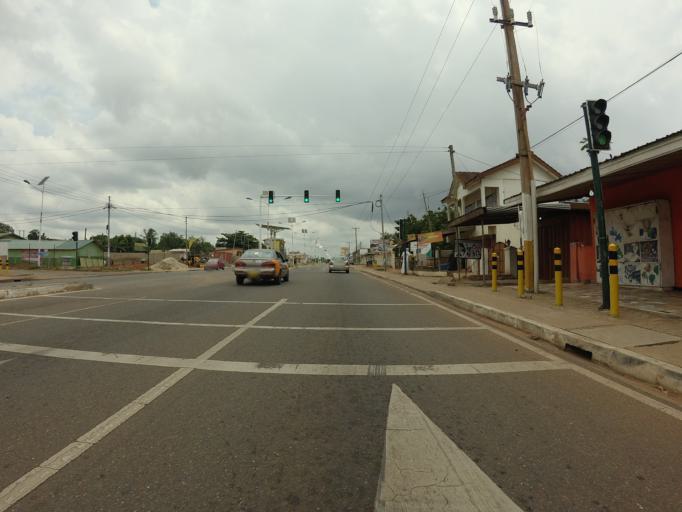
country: GH
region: Greater Accra
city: Medina Estates
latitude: 5.6621
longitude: -0.1514
